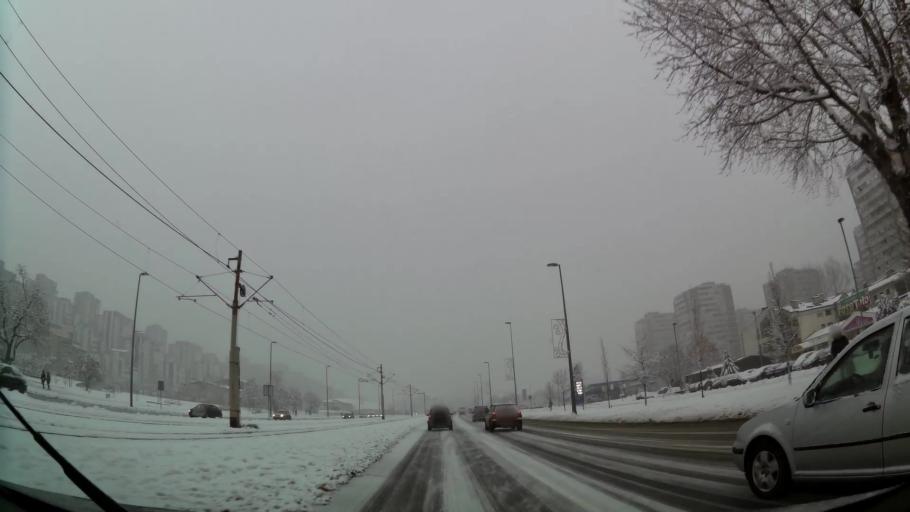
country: RS
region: Central Serbia
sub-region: Belgrade
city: Cukarica
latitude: 44.8002
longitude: 20.3770
